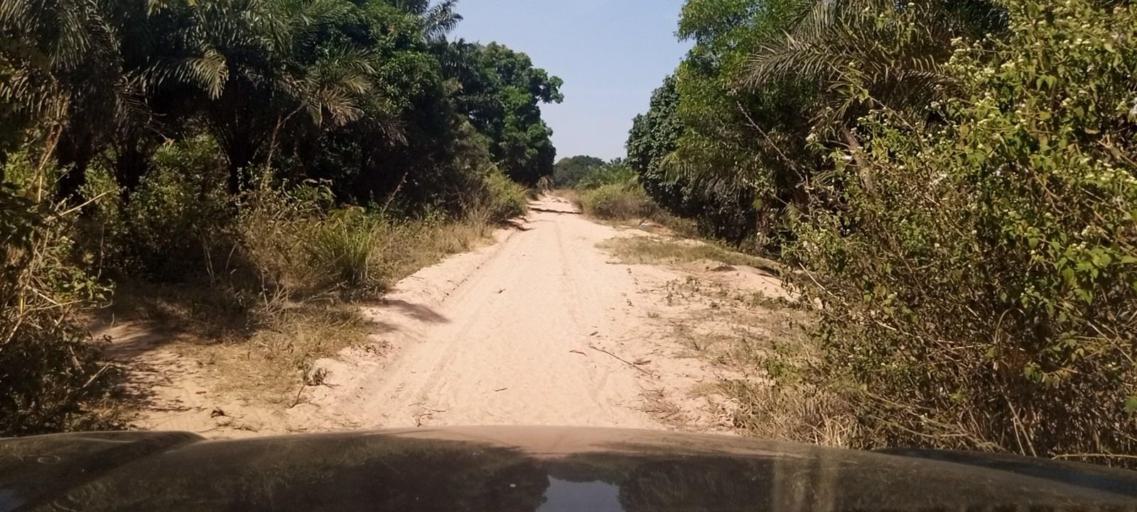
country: CD
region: Kasai-Oriental
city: Kabinda
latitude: -5.8036
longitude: 25.0142
